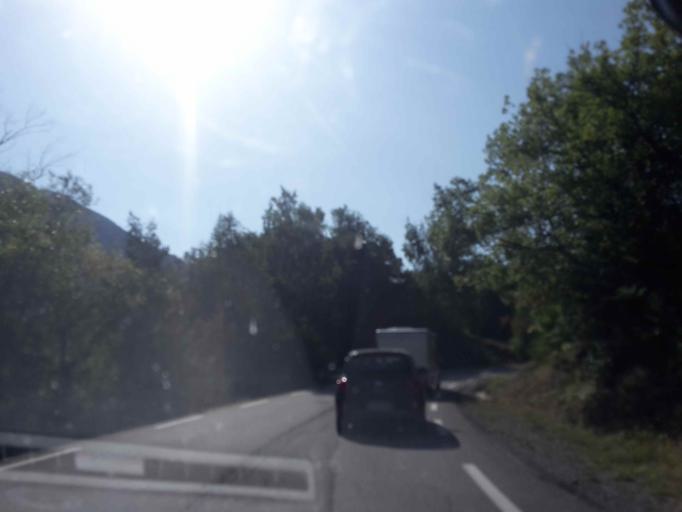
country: FR
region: Provence-Alpes-Cote d'Azur
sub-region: Departement des Hautes-Alpes
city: Guillestre
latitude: 44.6541
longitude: 6.6518
